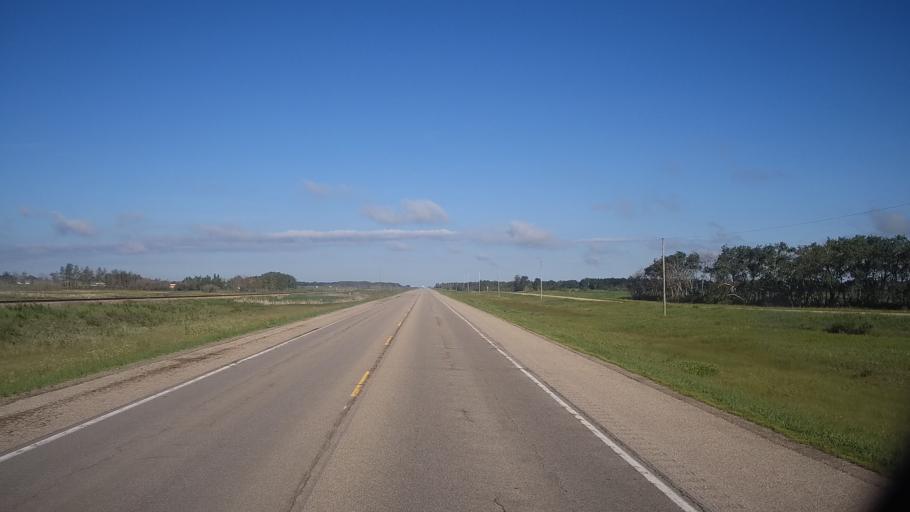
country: CA
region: Saskatchewan
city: Lanigan
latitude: 51.8520
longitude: -105.0696
